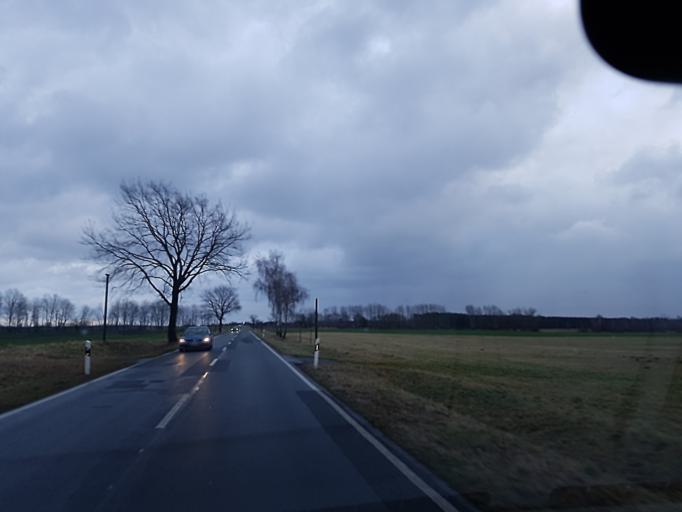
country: DE
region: Brandenburg
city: Hohenleipisch
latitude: 51.5330
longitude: 13.5989
